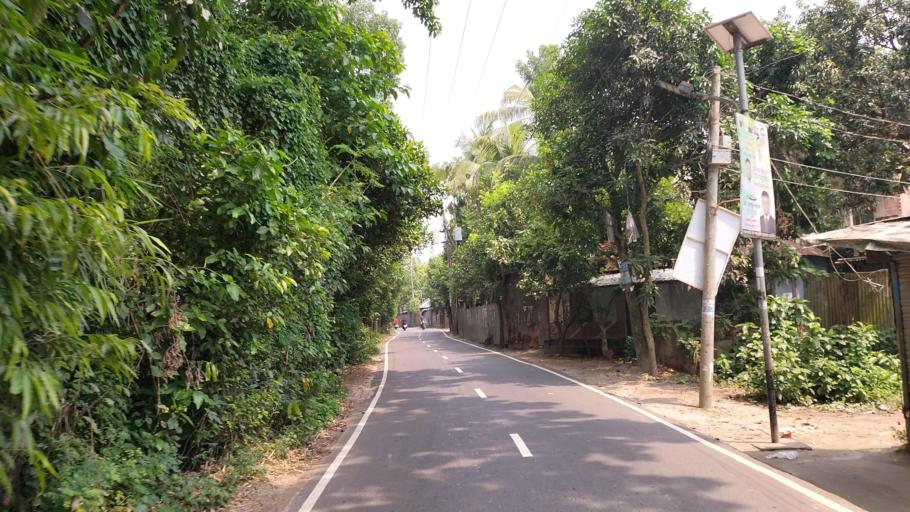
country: BD
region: Dhaka
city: Azimpur
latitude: 23.7152
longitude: 90.2789
